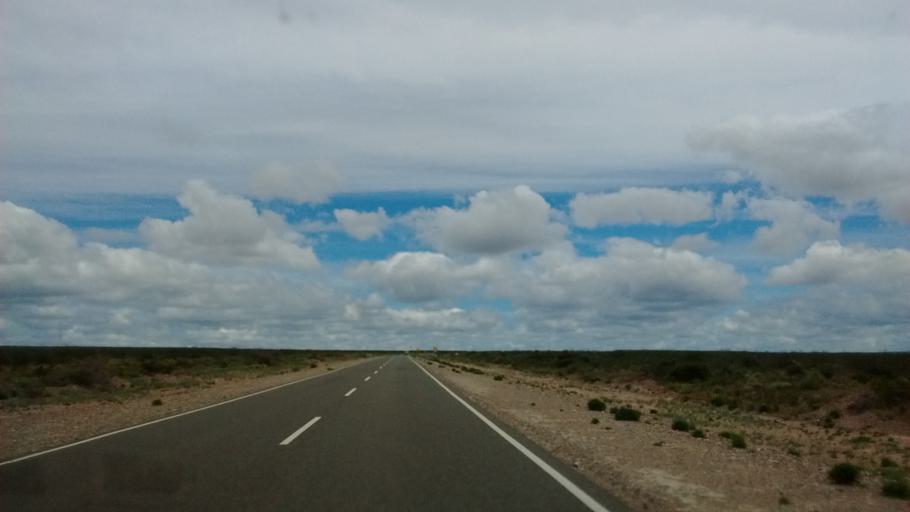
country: AR
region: Neuquen
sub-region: Departamento de Picun Leufu
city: Picun Leufu
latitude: -39.7461
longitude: -69.6134
